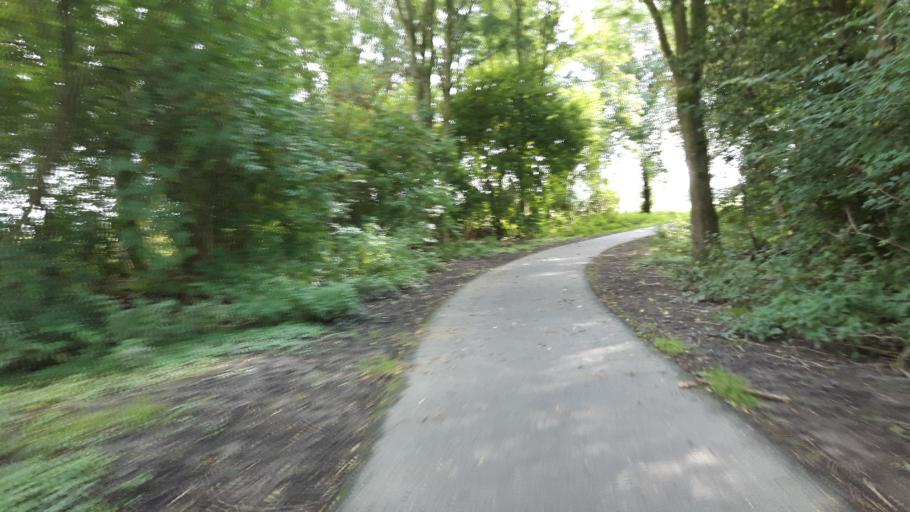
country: NL
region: North Holland
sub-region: Gemeente Medemblik
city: Medemblik
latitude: 52.7233
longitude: 5.1175
